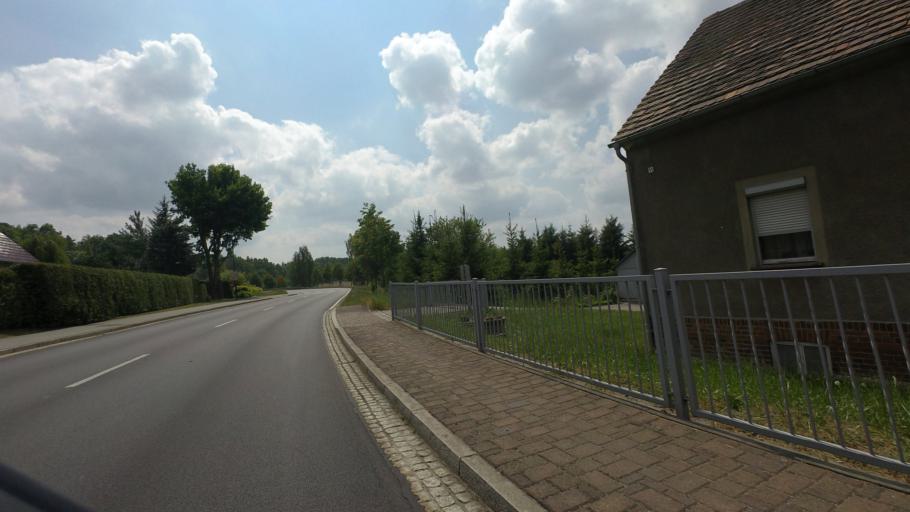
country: DE
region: Saxony
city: Rietschen
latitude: 51.3565
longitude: 14.8027
